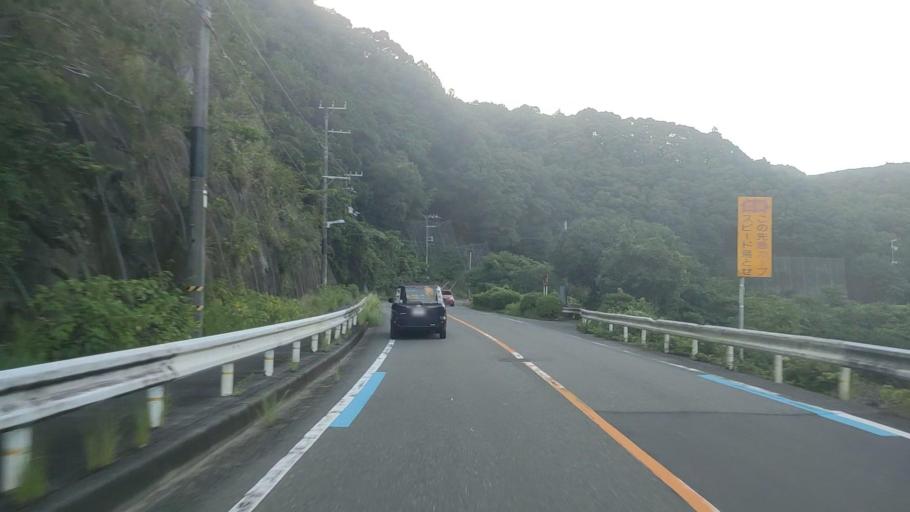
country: JP
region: Wakayama
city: Tanabe
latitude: 33.7975
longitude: 135.5197
